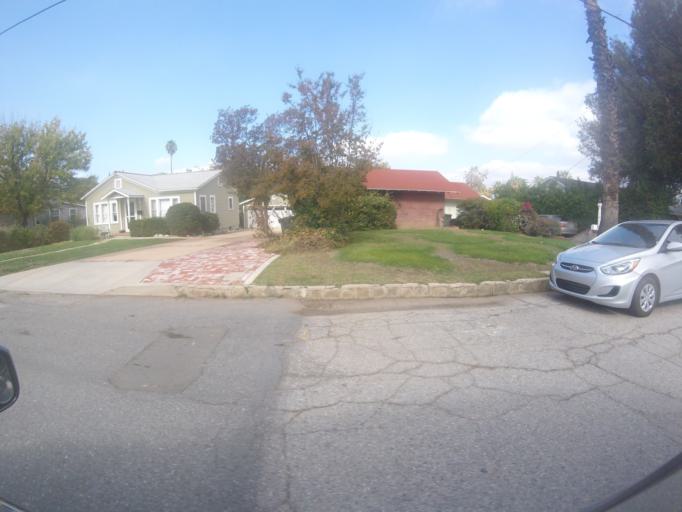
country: US
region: California
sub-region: San Bernardino County
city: Redlands
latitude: 34.0380
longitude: -117.1830
